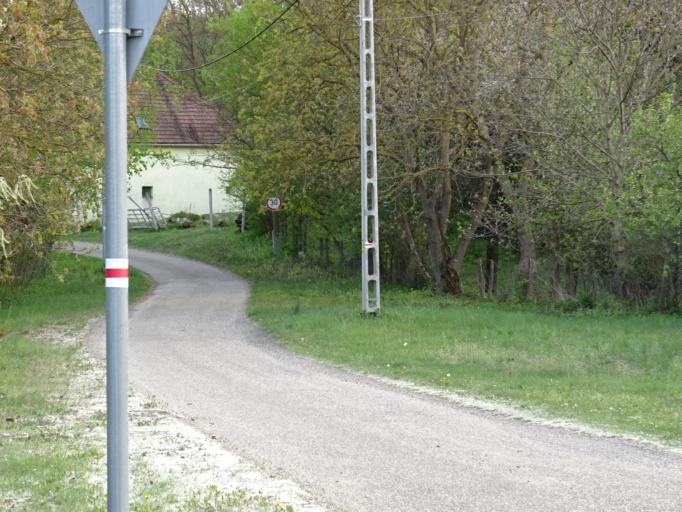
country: HU
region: Borsod-Abauj-Zemplen
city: Satoraljaujhely
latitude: 48.4600
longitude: 21.5900
